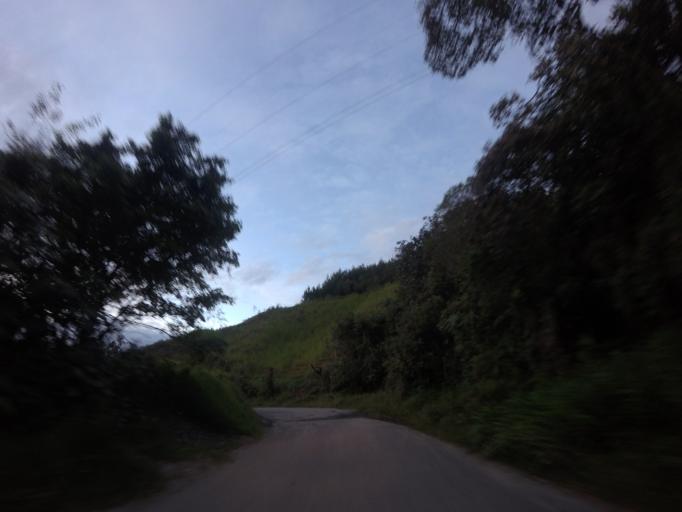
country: CO
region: Caldas
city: Manzanares
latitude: 5.2704
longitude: -75.1346
